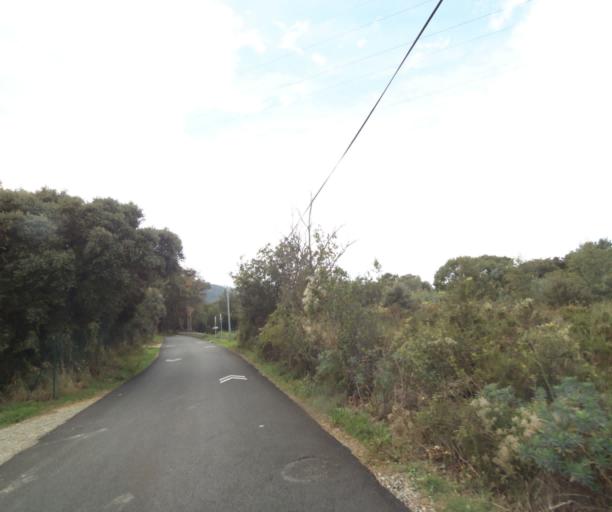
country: FR
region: Languedoc-Roussillon
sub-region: Departement des Pyrenees-Orientales
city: Argelers
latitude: 42.5419
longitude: 3.0076
